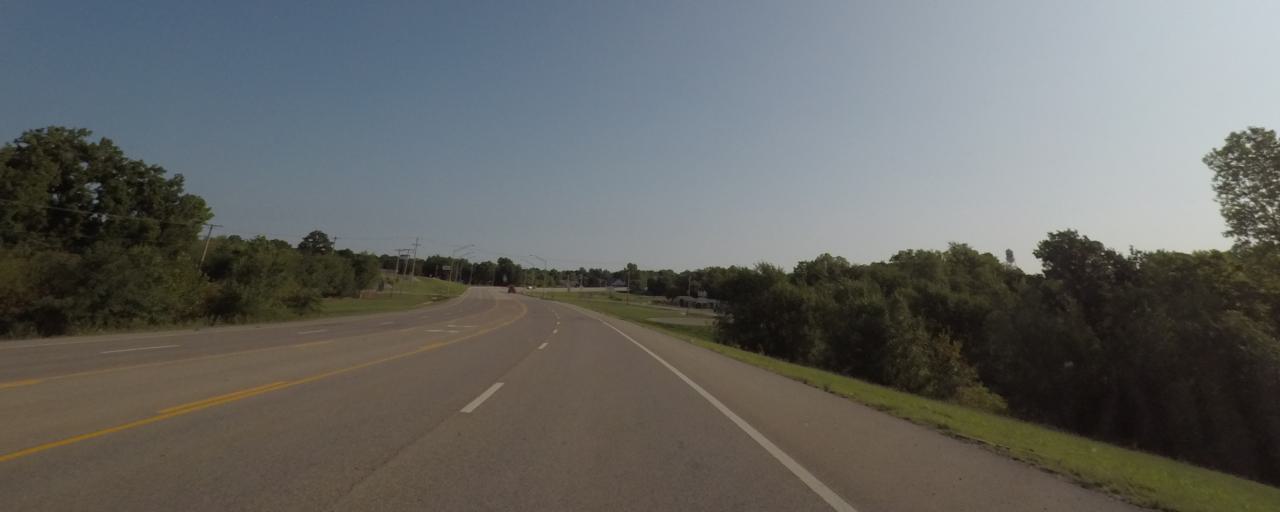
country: US
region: Oklahoma
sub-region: McClain County
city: Blanchard
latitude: 35.1331
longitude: -97.6651
